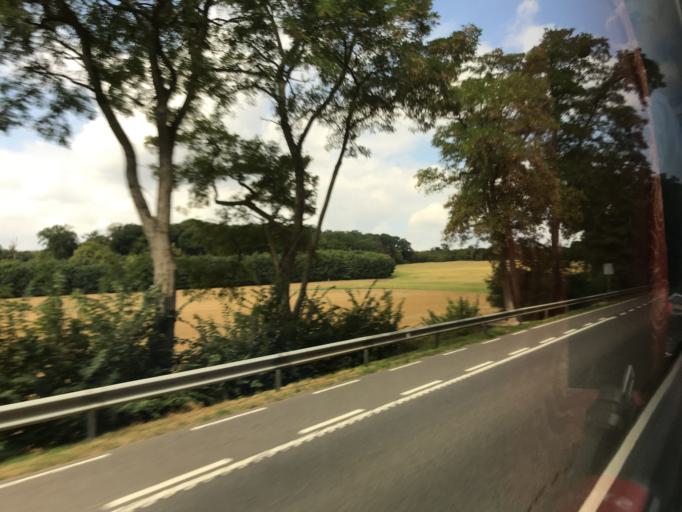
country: LU
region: Luxembourg
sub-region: Canton d'Esch-sur-Alzette
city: Roeser
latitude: 49.5415
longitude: 6.1754
